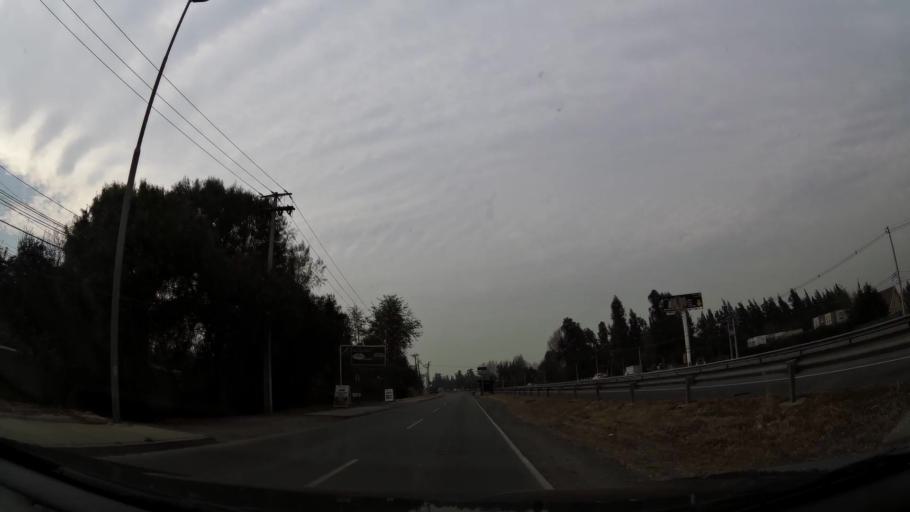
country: CL
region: Santiago Metropolitan
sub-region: Provincia de Chacabuco
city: Chicureo Abajo
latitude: -33.2704
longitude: -70.7006
